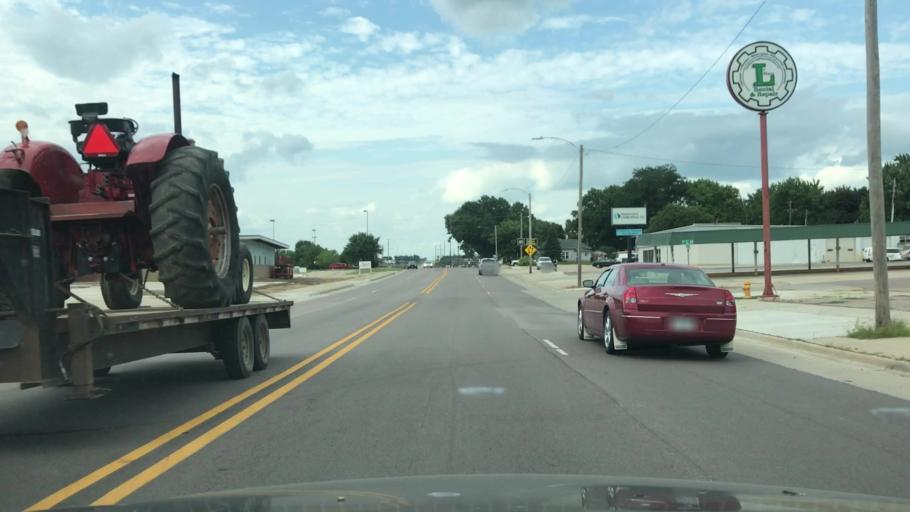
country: US
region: Iowa
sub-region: Plymouth County
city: Le Mars
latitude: 42.7952
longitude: -96.1738
